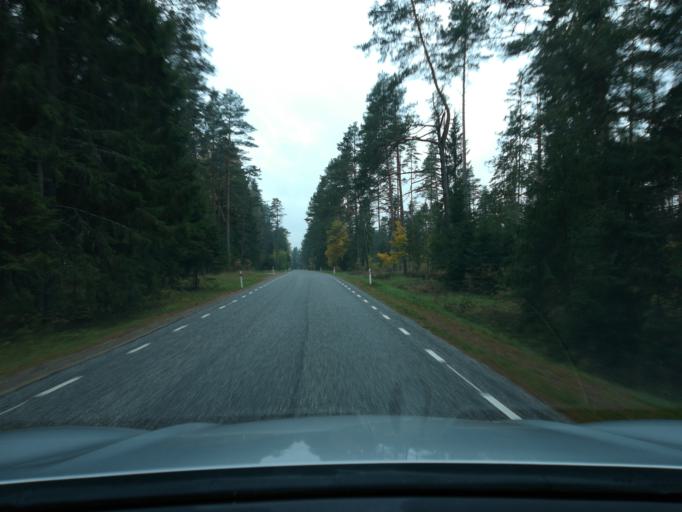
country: EE
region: Ida-Virumaa
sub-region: Johvi vald
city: Johvi
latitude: 59.1539
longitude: 27.3874
